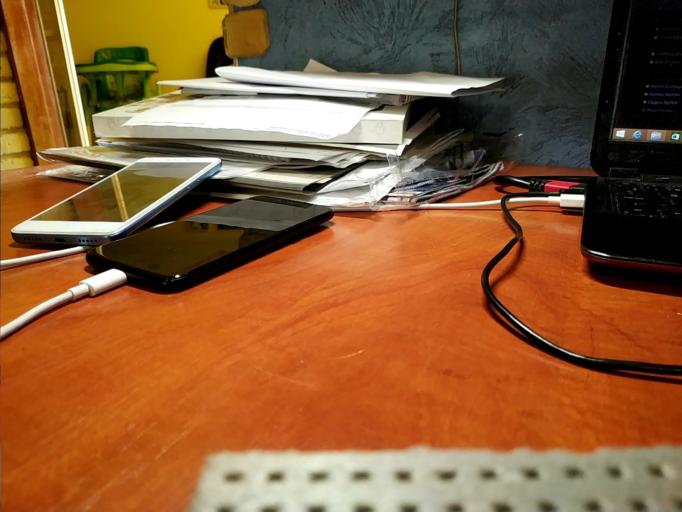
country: RU
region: Tverskaya
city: Spirovo
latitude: 57.4252
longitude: 35.0789
